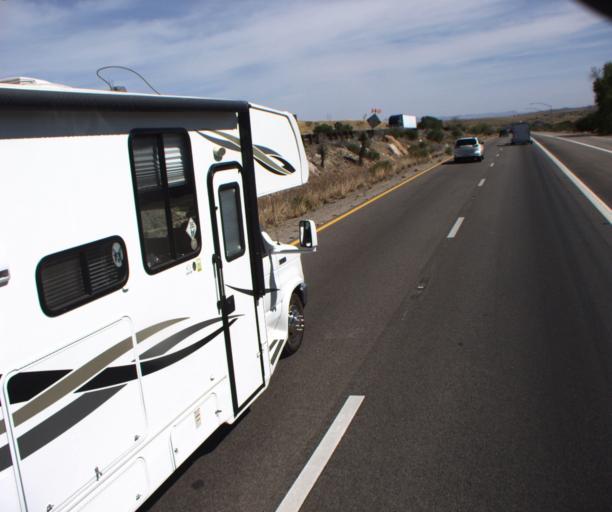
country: US
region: Arizona
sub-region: Cochise County
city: Saint David
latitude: 32.0631
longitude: -110.0741
